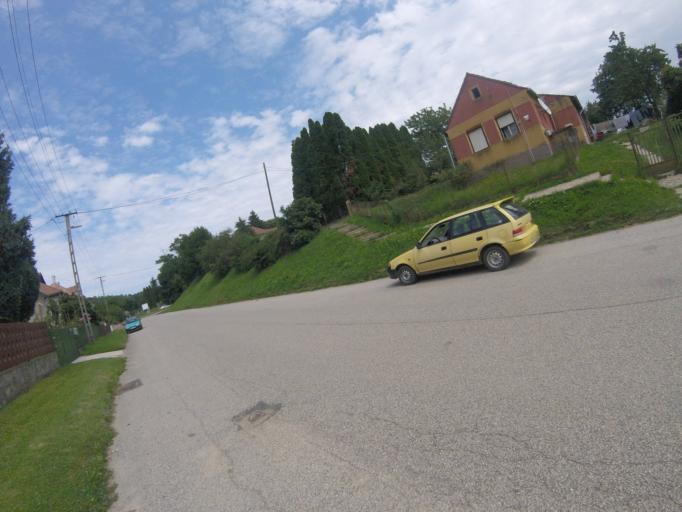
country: HR
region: Medimurska
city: Podturen
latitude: 46.5414
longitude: 16.5929
